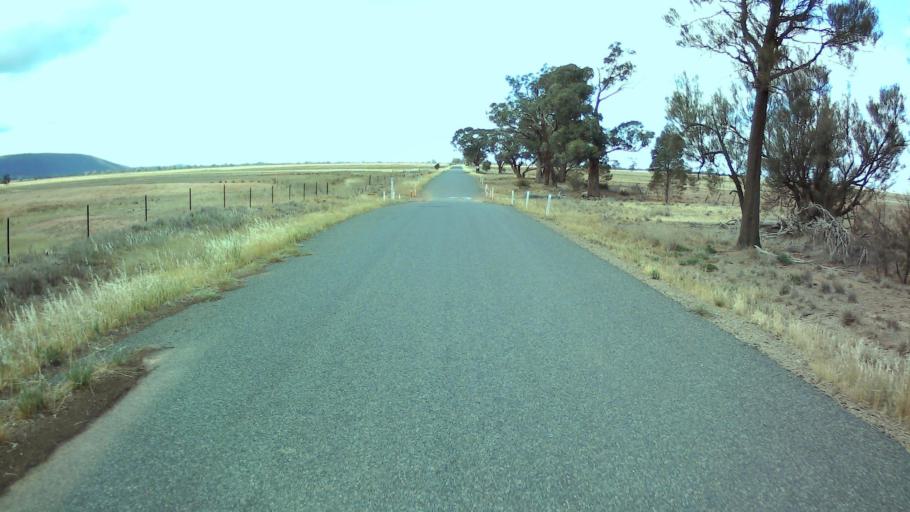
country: AU
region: New South Wales
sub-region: Weddin
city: Grenfell
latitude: -33.8661
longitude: 147.9273
